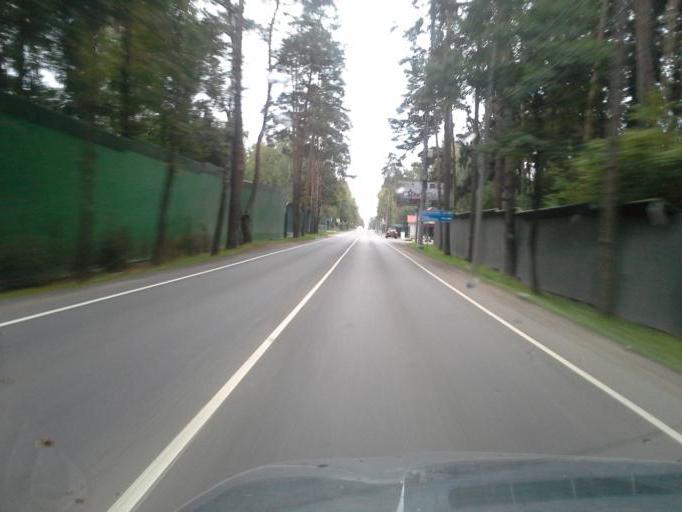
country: RU
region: Moskovskaya
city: Nazar'yevo
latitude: 55.6993
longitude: 37.0643
